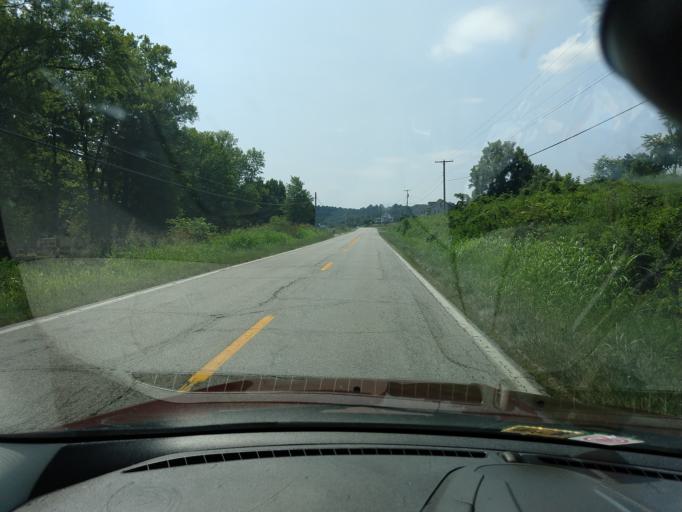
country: US
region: West Virginia
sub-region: Mason County
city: New Haven
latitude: 38.8818
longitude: -81.9255
